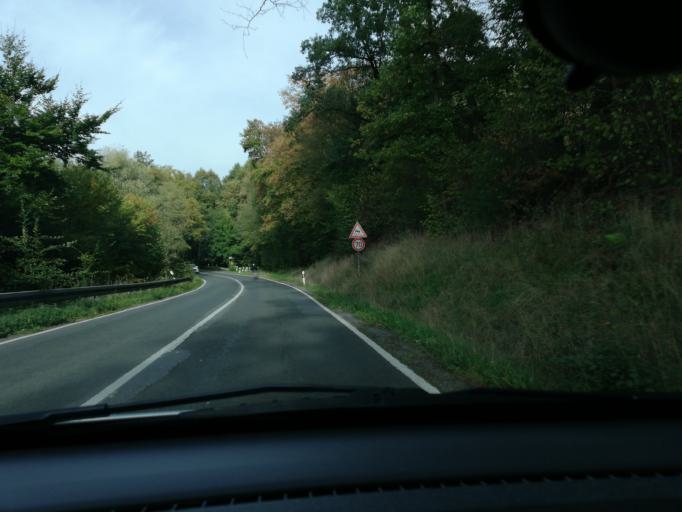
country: DE
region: North Rhine-Westphalia
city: Sprockhovel
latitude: 51.3522
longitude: 7.2547
